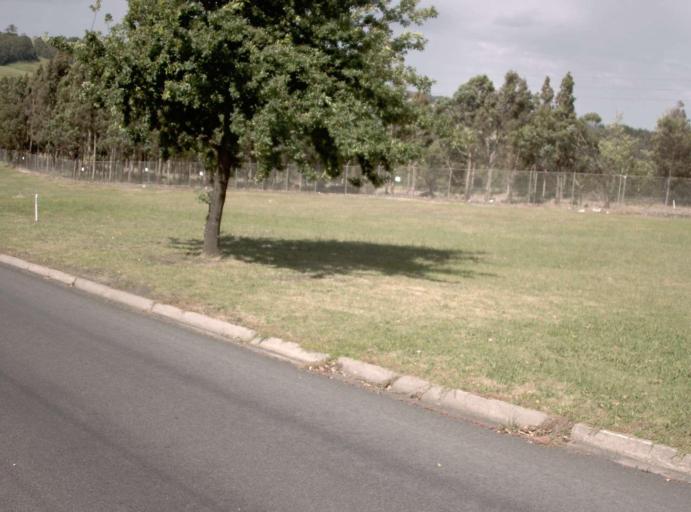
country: AU
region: Victoria
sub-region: Latrobe
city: Morwell
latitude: -38.1631
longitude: 146.3667
